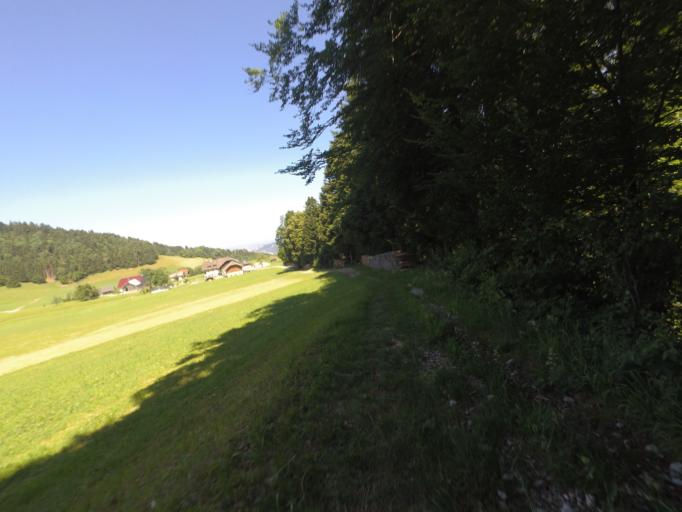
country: AT
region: Salzburg
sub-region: Politischer Bezirk Salzburg-Umgebung
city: Elsbethen
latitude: 47.7598
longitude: 13.1098
